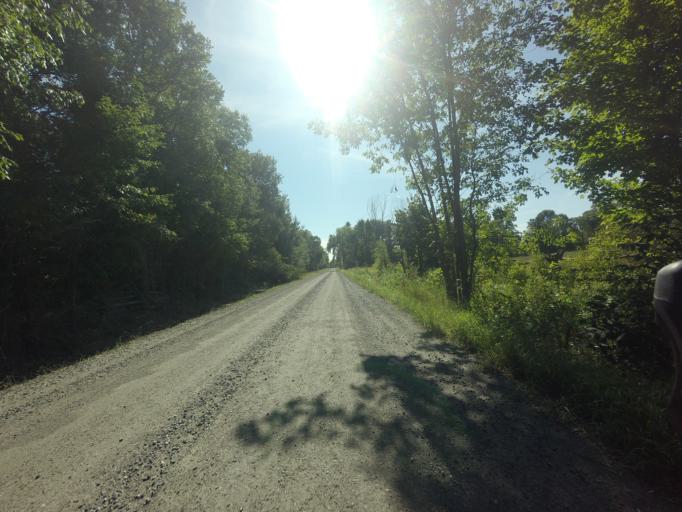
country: CA
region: Ontario
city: Perth
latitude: 44.9518
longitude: -76.3539
